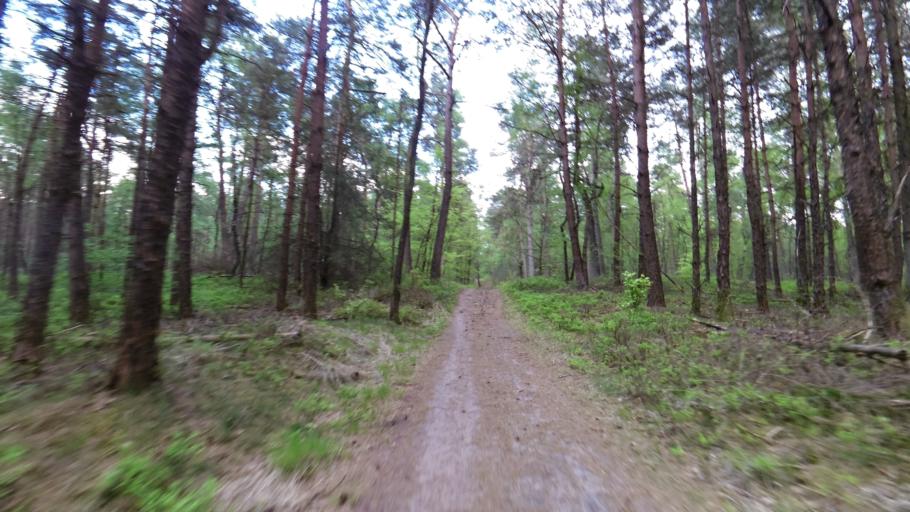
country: NL
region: Gelderland
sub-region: Gemeente Brummen
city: Eerbeek
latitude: 52.0818
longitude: 6.0372
